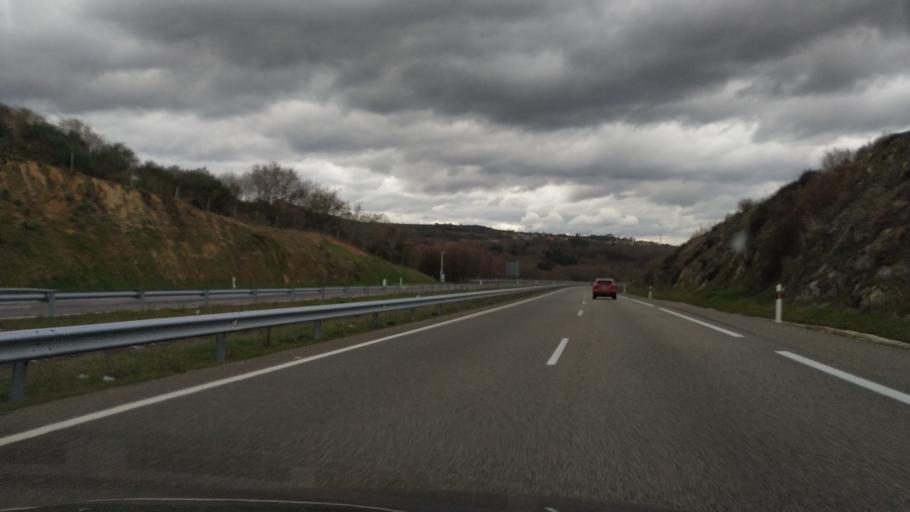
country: ES
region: Galicia
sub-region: Provincia de Ourense
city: Taboadela
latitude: 42.2145
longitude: -7.8376
